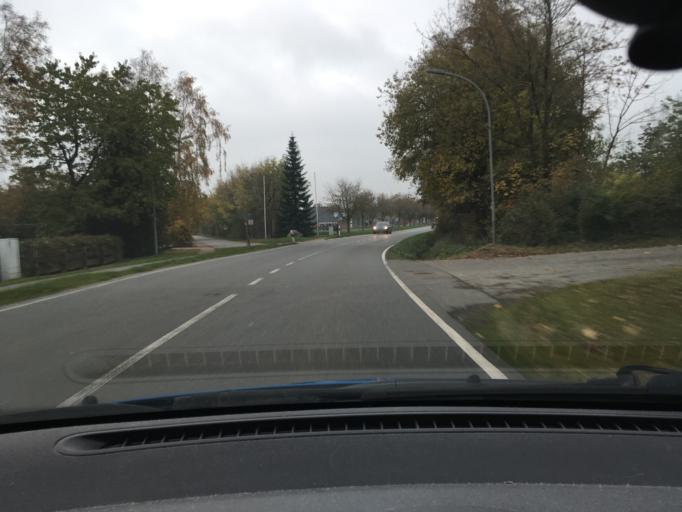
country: DE
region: Schleswig-Holstein
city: Horstedt
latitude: 54.5212
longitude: 9.0671
